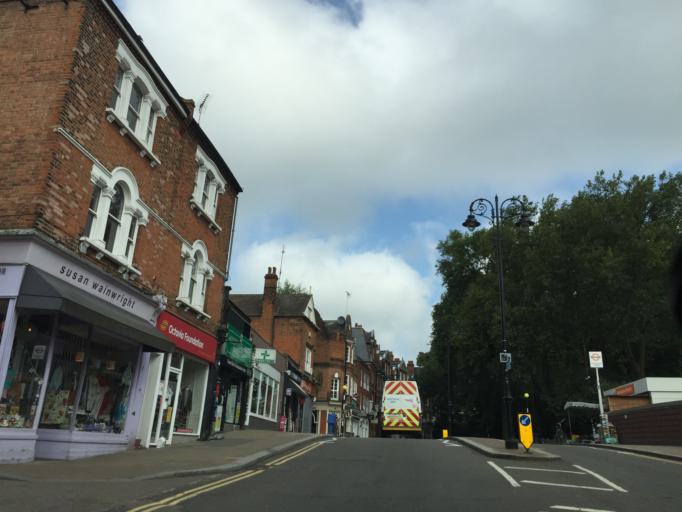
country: GB
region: England
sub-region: Greater London
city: Belsize Park
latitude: 51.5548
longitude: -0.1659
